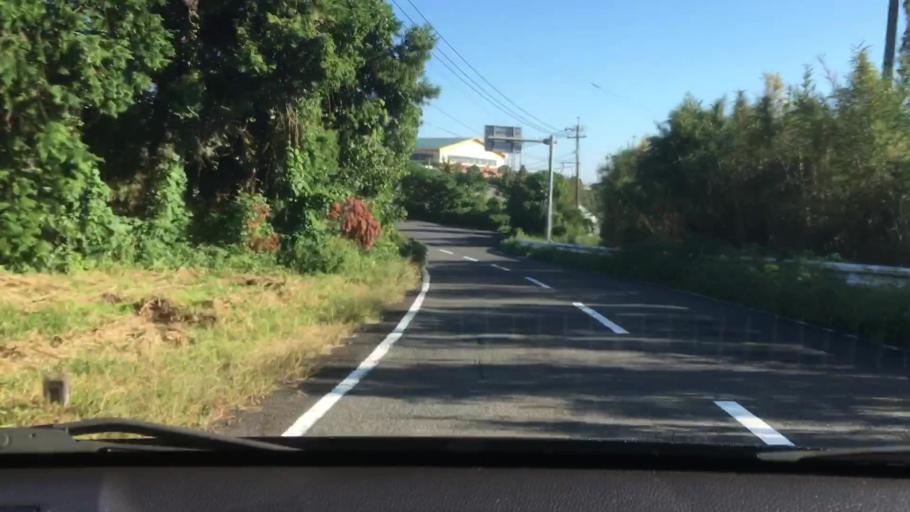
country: JP
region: Nagasaki
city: Sasebo
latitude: 33.0408
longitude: 129.6957
